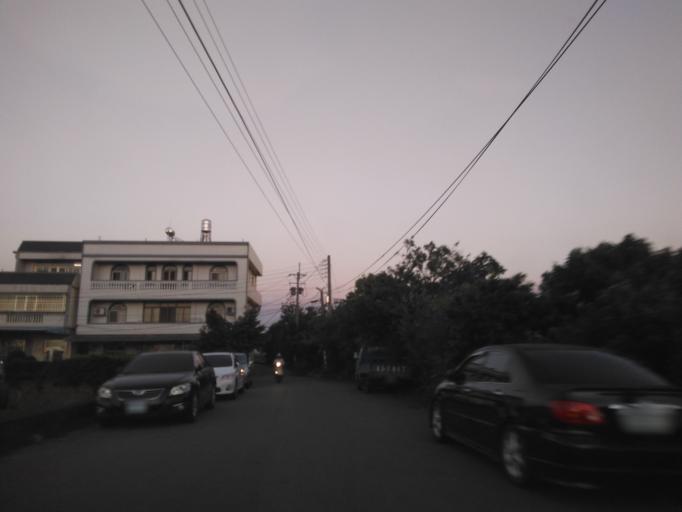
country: TW
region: Taiwan
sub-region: Changhua
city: Chang-hua
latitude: 24.0847
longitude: 120.5909
